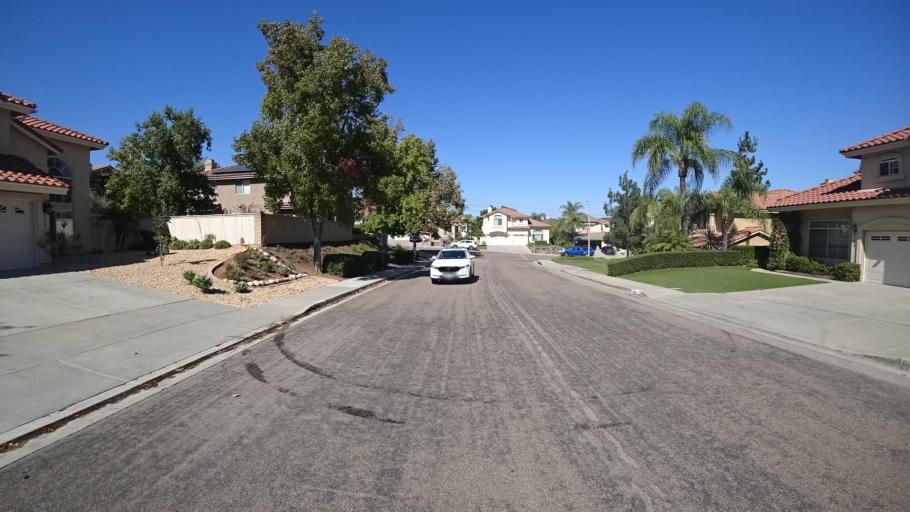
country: US
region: California
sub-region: San Diego County
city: Rancho San Diego
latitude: 32.7361
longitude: -116.9130
